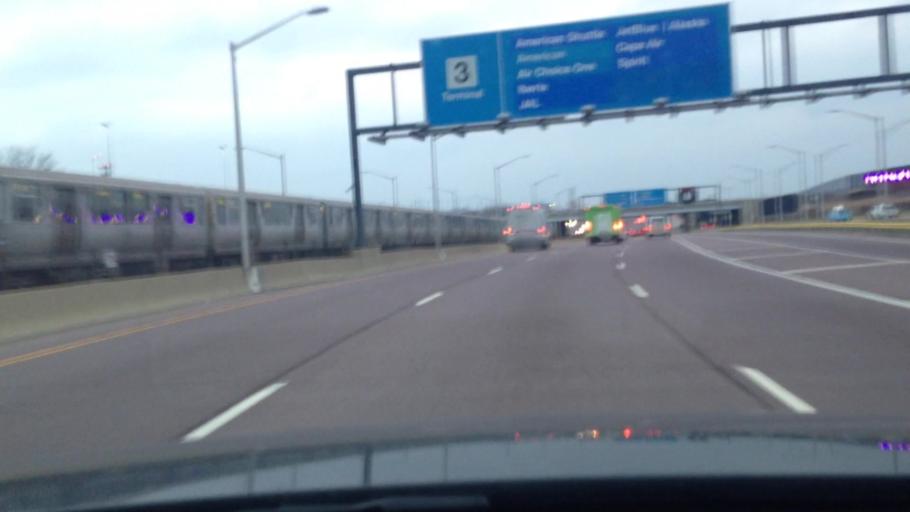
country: US
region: Illinois
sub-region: Cook County
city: Rosemont
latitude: 41.9778
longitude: -87.8916
